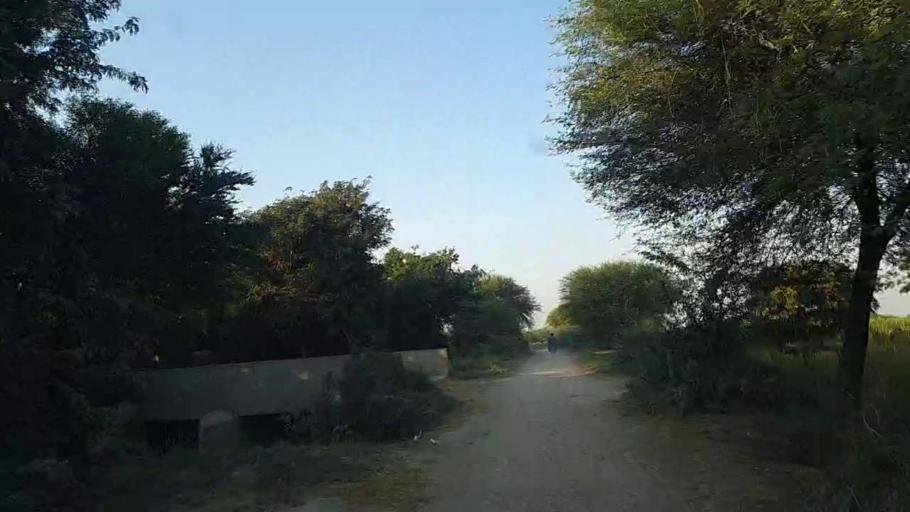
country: PK
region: Sindh
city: Mirpur Batoro
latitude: 24.7133
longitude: 68.2145
